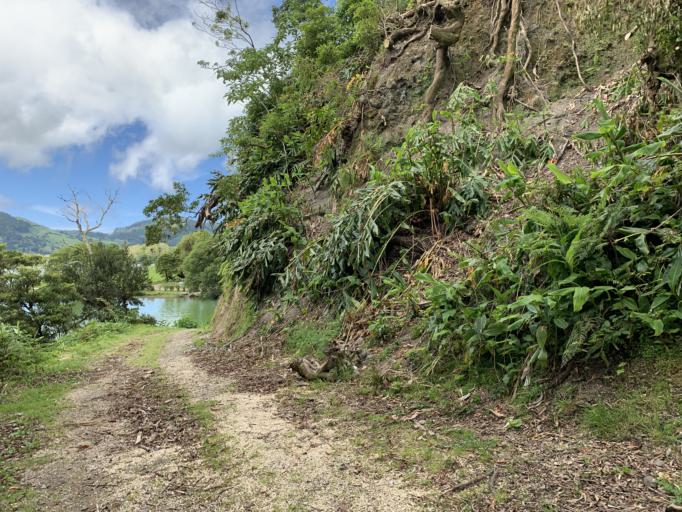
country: PT
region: Azores
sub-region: Ponta Delgada
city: Arrifes
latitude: 37.8481
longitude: -25.7849
